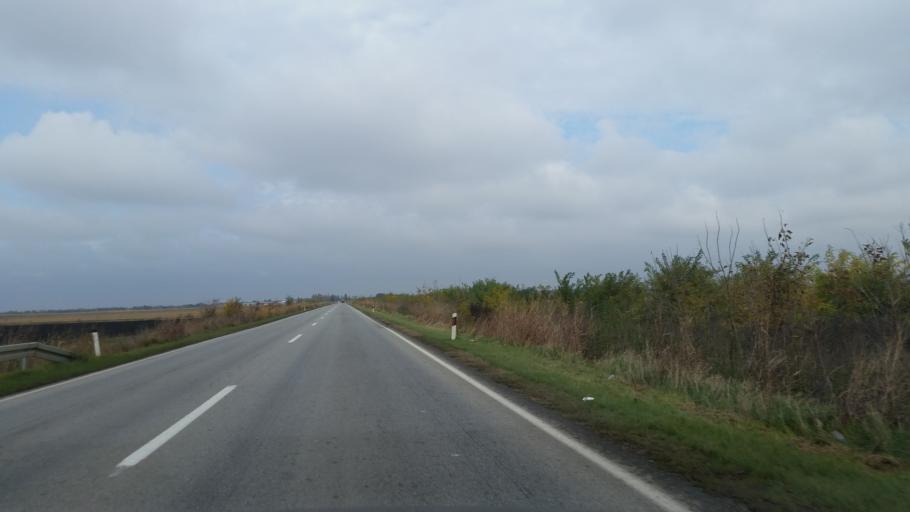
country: RS
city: Melenci
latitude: 45.4913
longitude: 20.3296
